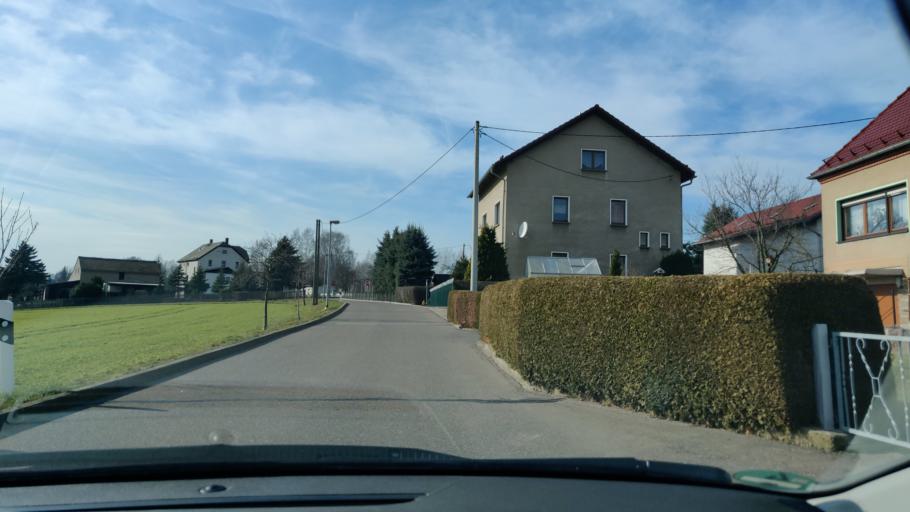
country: DE
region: Saxony
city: Narsdorf
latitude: 51.0091
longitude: 12.7173
